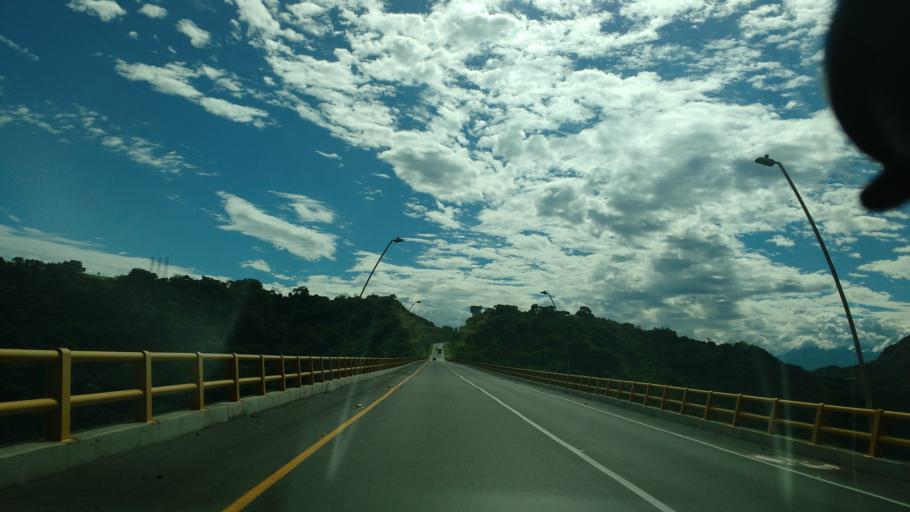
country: CO
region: Tolima
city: Valle de San Juan
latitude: 4.2905
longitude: -75.0325
